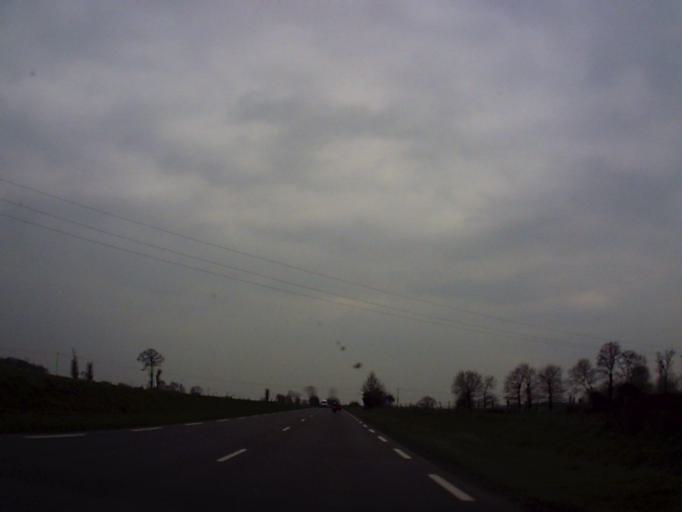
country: FR
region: Brittany
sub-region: Departement d'Ille-et-Vilaine
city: Pace
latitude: 48.1302
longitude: -1.7718
